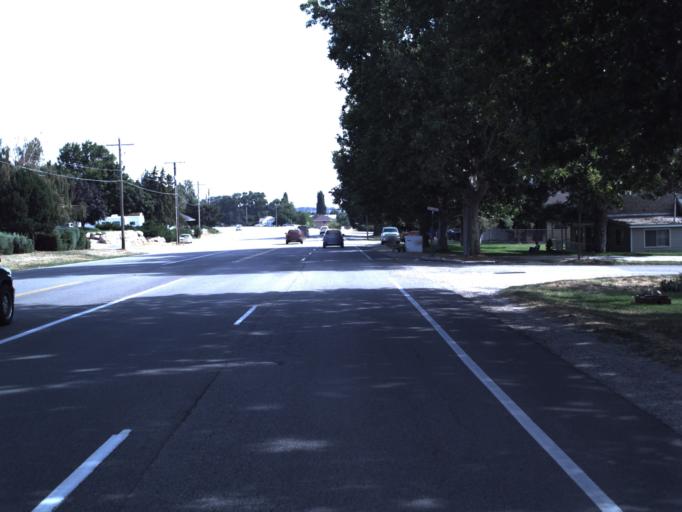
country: US
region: Utah
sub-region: Box Elder County
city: Willard
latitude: 41.4073
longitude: -112.0364
